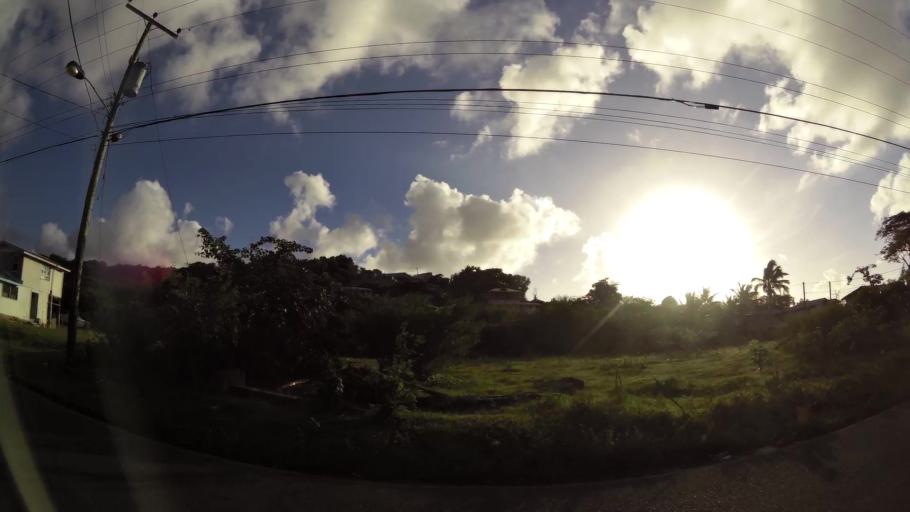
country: LC
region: Gros-Islet
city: Gros Islet
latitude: 14.0778
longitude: -60.9429
